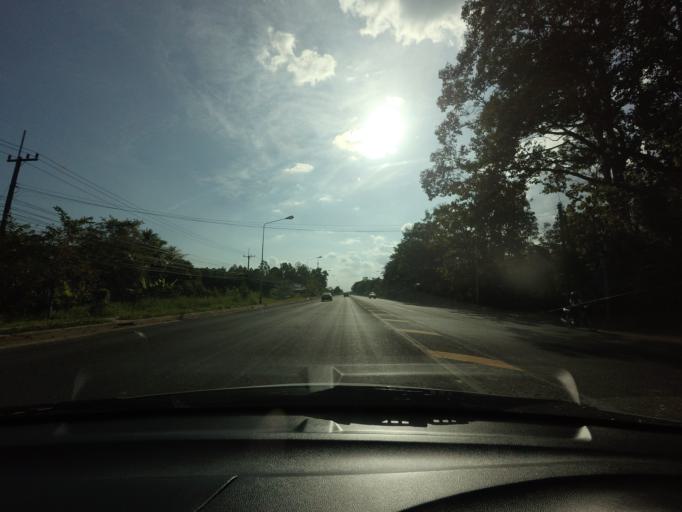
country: TH
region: Nakhon Nayok
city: Nakhon Nayok
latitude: 14.2649
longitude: 101.2702
